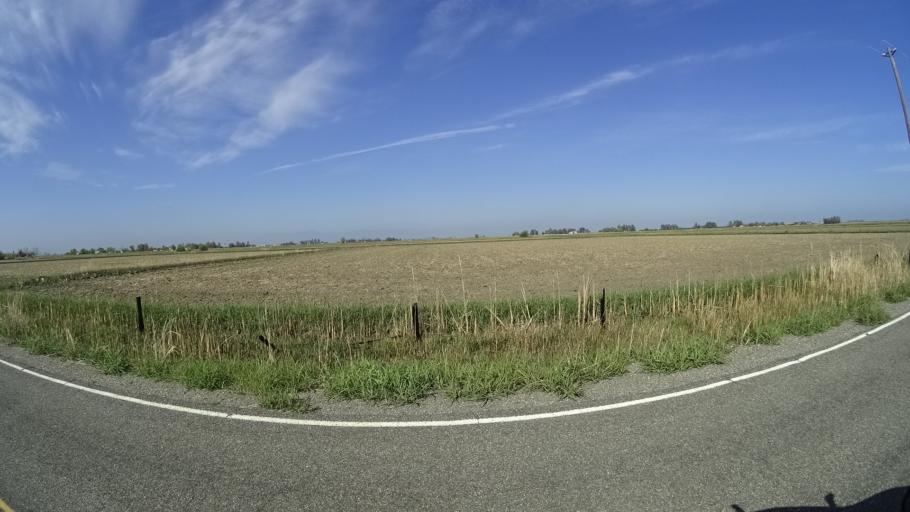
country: US
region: California
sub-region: Glenn County
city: Hamilton City
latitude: 39.5899
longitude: -122.0370
